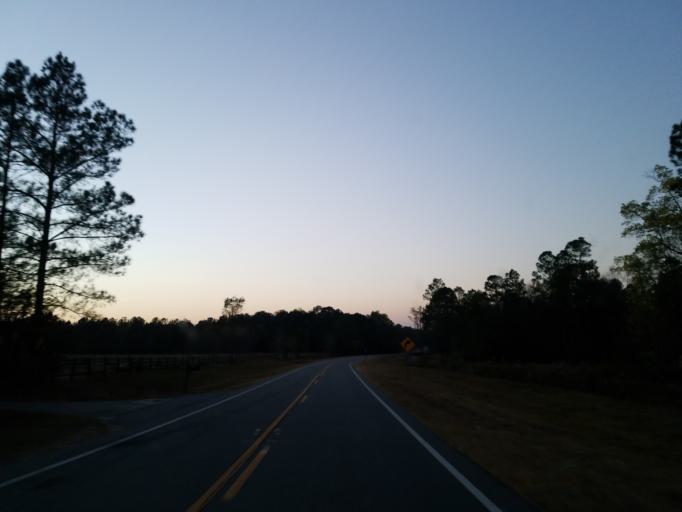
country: US
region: Georgia
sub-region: Wilcox County
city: Rochelle
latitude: 31.8168
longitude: -83.5333
